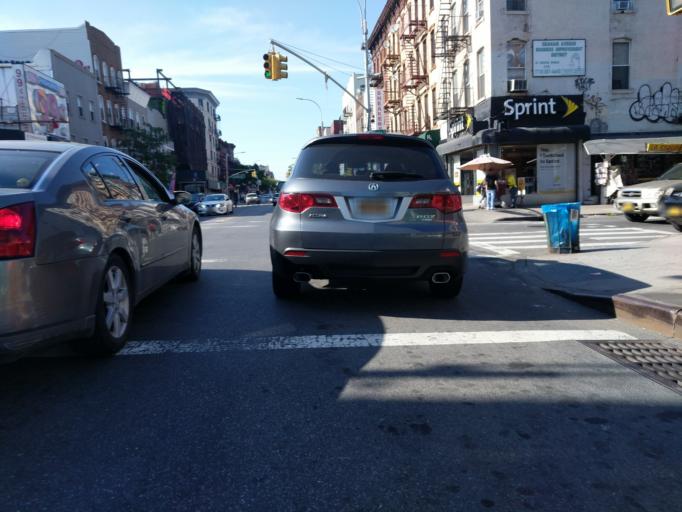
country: US
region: New York
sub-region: Queens County
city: Long Island City
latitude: 40.7037
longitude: -73.9426
